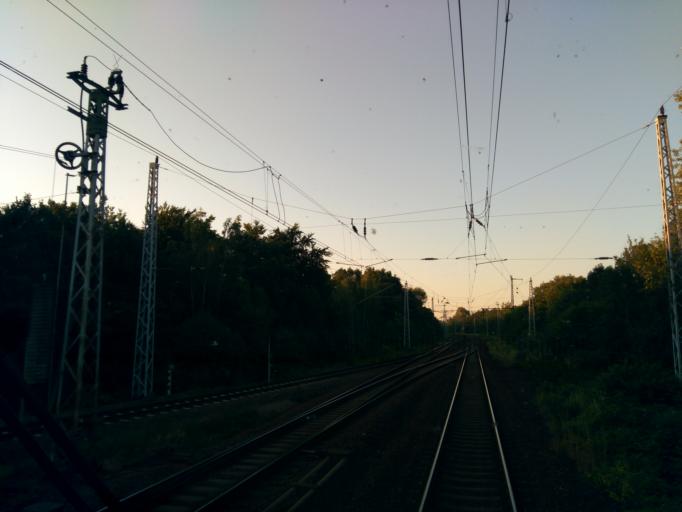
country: DE
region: Berlin
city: Karlshorst
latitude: 52.4639
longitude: 13.5513
